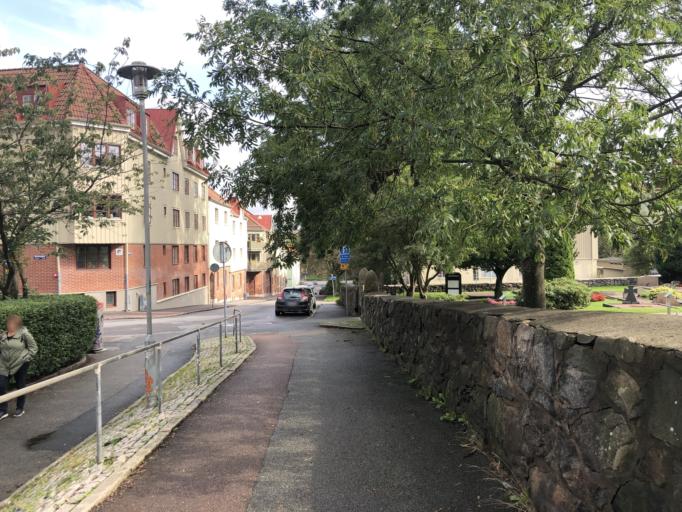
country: SE
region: Vaestra Goetaland
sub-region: Goteborg
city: Majorna
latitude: 57.6931
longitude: 11.9227
